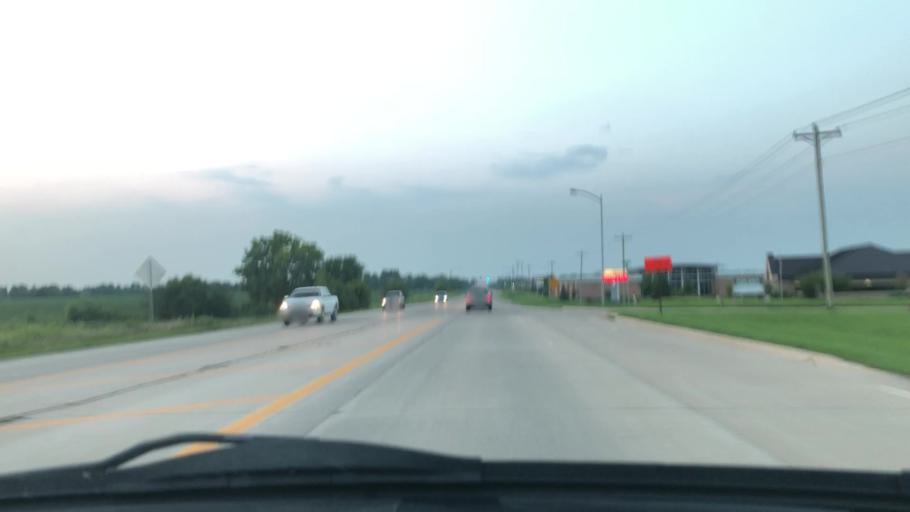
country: US
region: Iowa
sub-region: Johnson County
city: North Liberty
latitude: 41.7248
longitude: -91.6077
